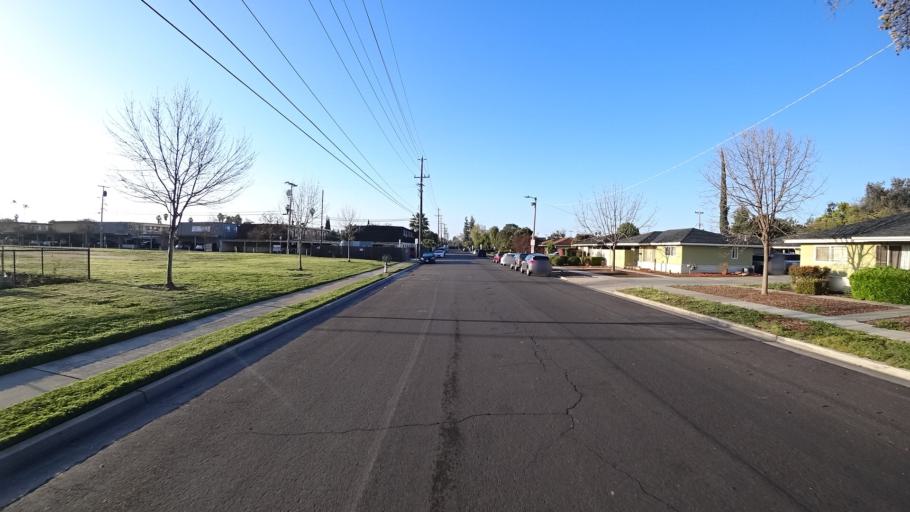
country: US
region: California
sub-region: Fresno County
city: Clovis
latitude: 36.8150
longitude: -119.7655
